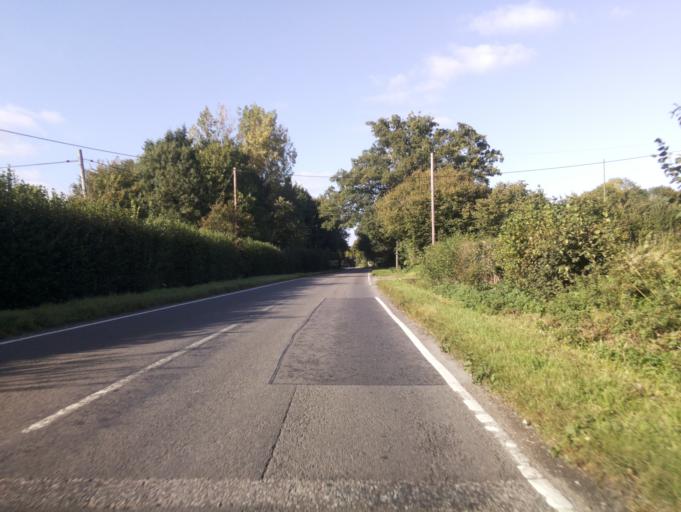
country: GB
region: England
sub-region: Hampshire
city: Alton
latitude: 51.1051
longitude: -0.9936
